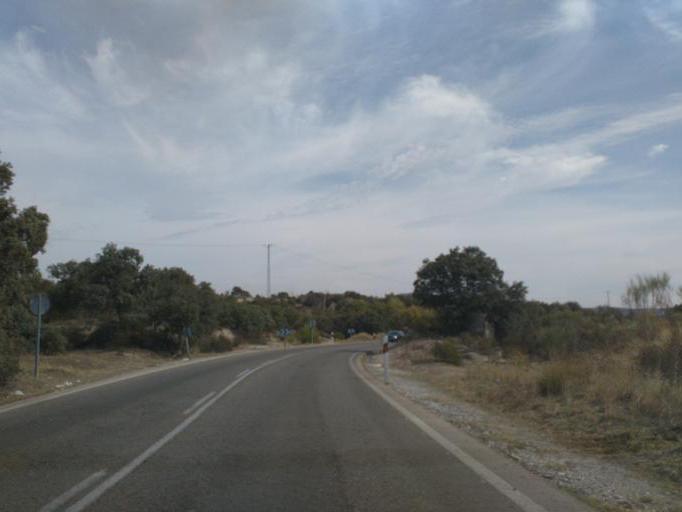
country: ES
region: Madrid
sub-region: Provincia de Madrid
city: Galapagar
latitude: 40.5811
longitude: -3.9806
